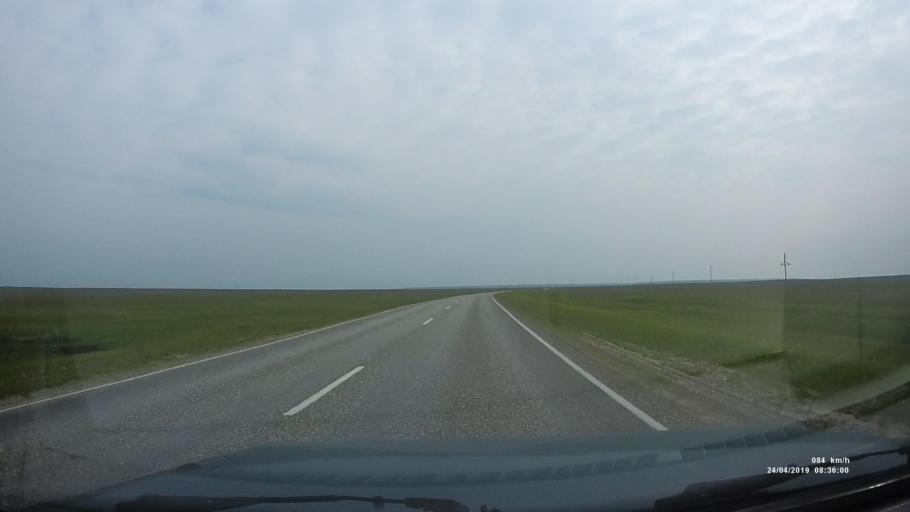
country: RU
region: Kalmykiya
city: Arshan'
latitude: 46.2019
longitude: 43.9273
